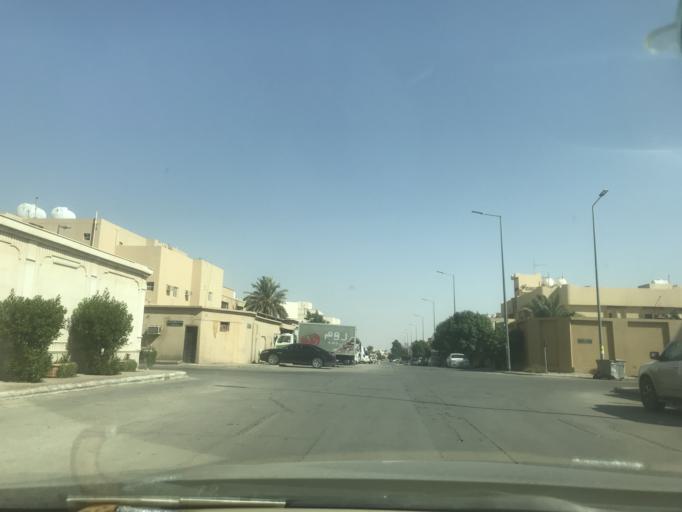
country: SA
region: Ar Riyad
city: Riyadh
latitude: 24.7338
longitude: 46.7645
